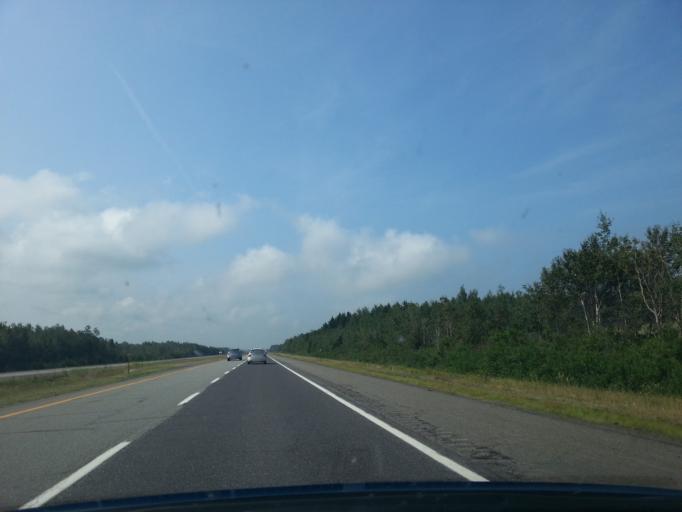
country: CA
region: Quebec
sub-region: Bas-Saint-Laurent
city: Riviere-du-Loup
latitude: 47.7614
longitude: -69.6005
